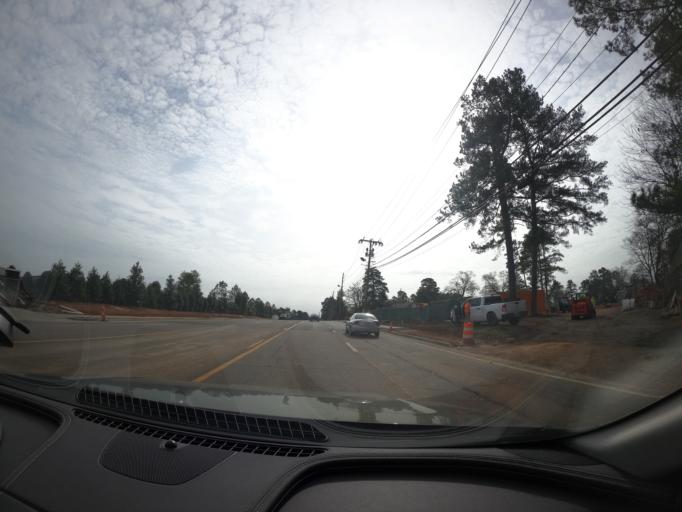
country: US
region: South Carolina
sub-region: Aiken County
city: North Augusta
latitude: 33.5024
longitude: -82.0145
